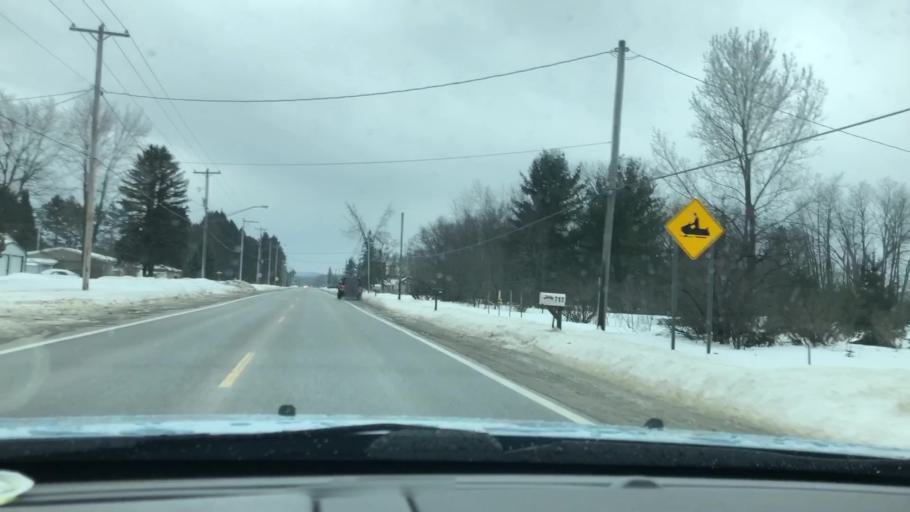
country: US
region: Michigan
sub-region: Charlevoix County
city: East Jordan
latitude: 45.1449
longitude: -85.1192
